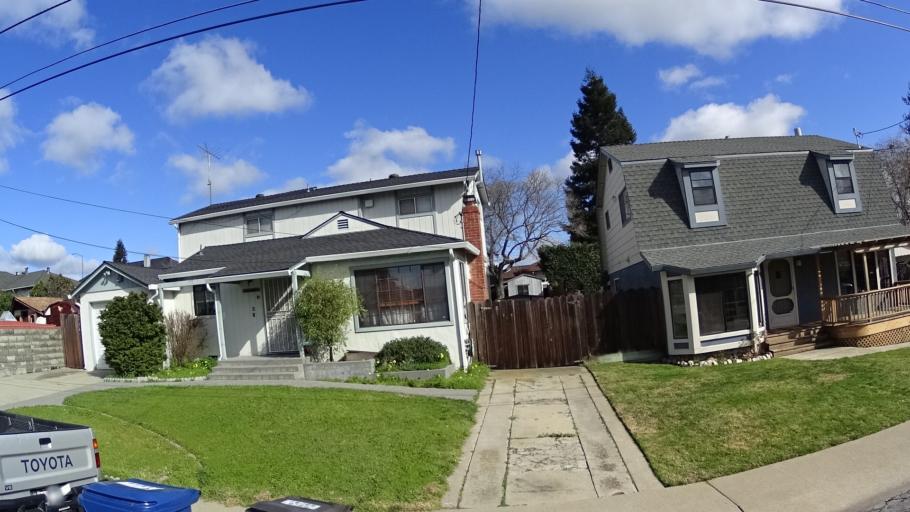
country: US
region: California
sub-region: Alameda County
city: Castro Valley
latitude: 37.6861
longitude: -122.0684
